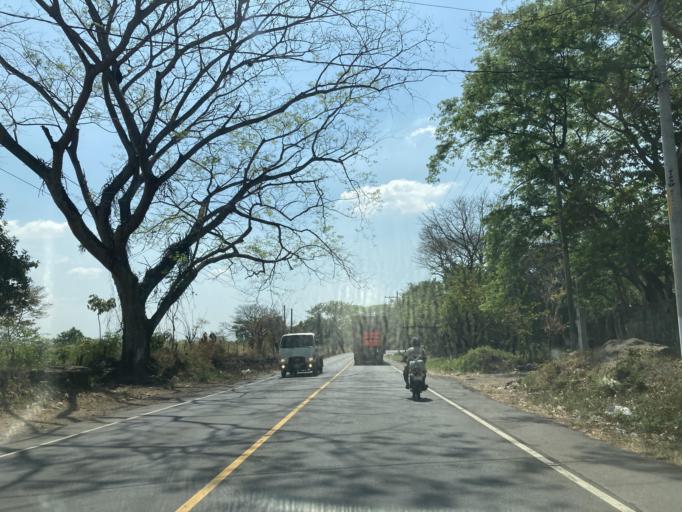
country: GT
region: Escuintla
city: Guanagazapa
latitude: 14.2154
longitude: -90.7243
